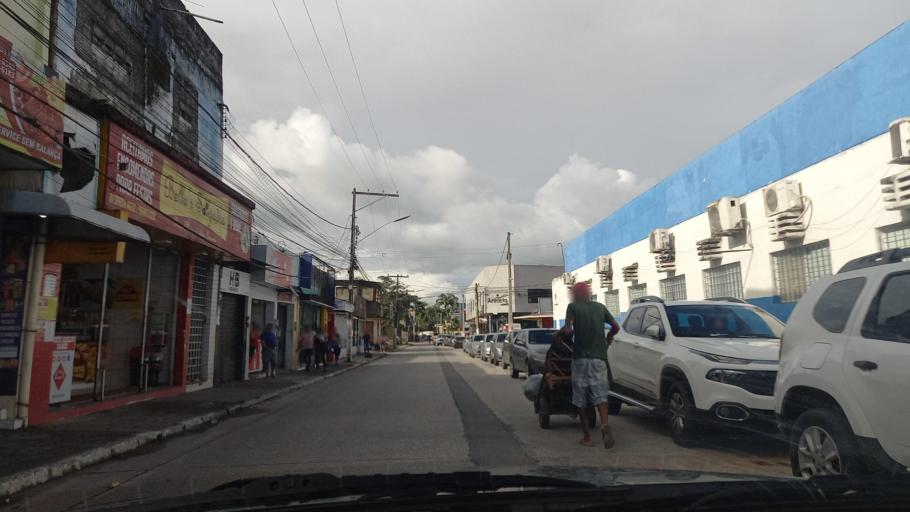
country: BR
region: Pernambuco
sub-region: Palmares
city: Palmares
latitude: -8.6841
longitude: -35.5885
